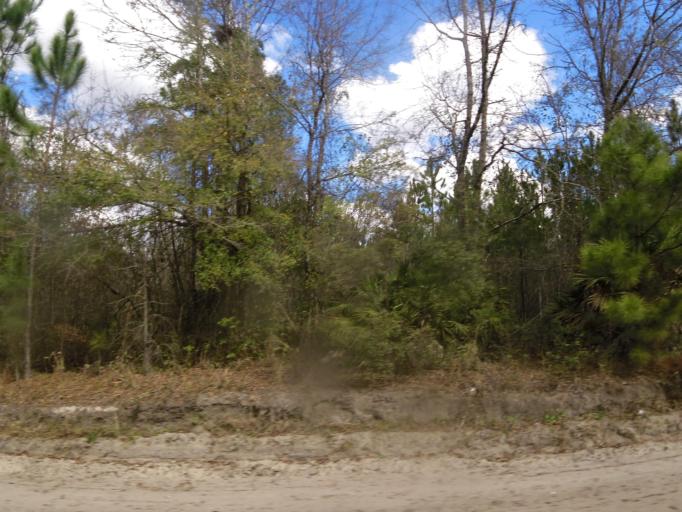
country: US
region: Florida
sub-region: Clay County
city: Green Cove Springs
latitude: 29.8367
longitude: -81.7900
